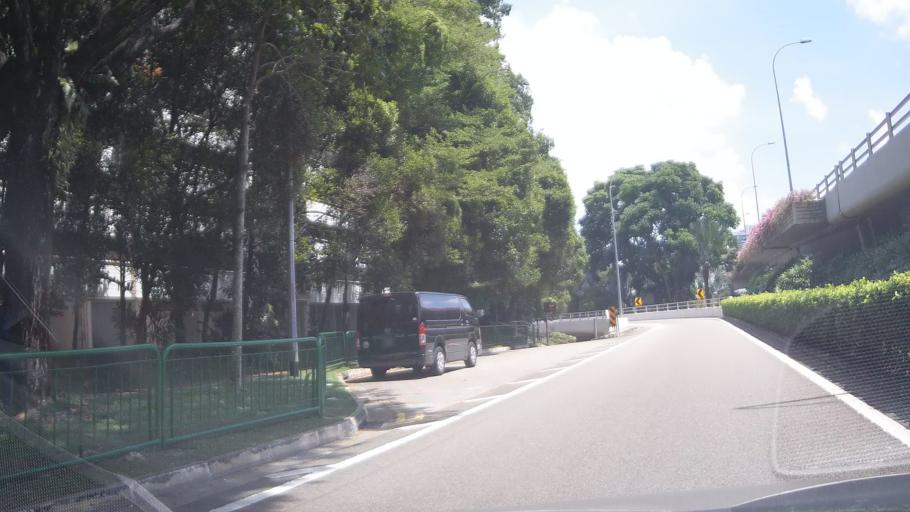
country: SG
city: Singapore
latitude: 1.3404
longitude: 103.7480
